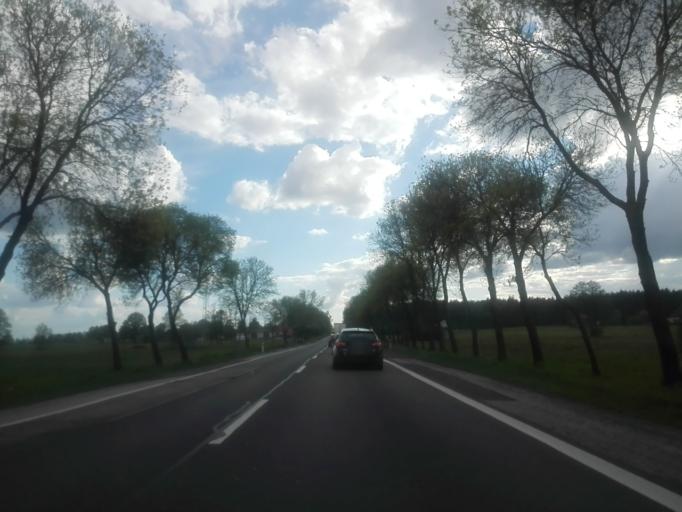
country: PL
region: Masovian Voivodeship
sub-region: Powiat wyszkowski
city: Dlugosiodlo
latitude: 52.7228
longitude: 21.7166
